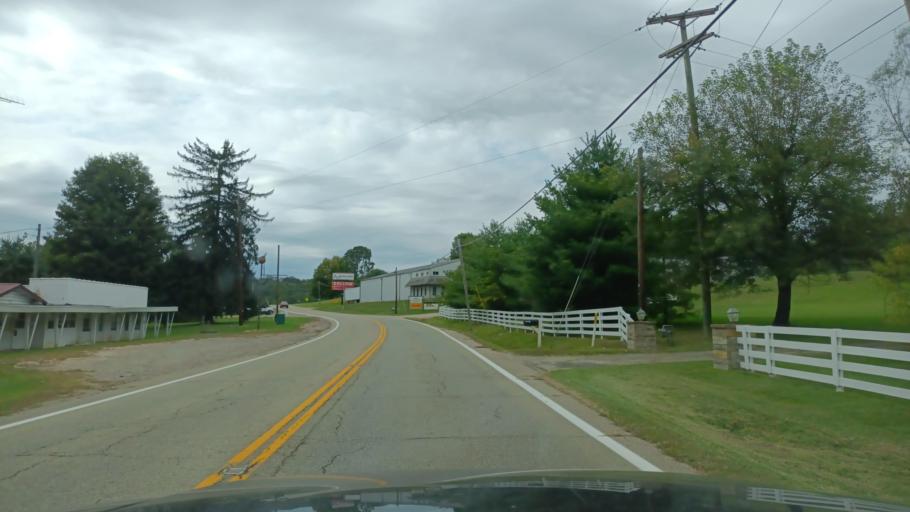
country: US
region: Ohio
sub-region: Vinton County
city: McArthur
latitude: 39.2624
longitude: -82.5076
